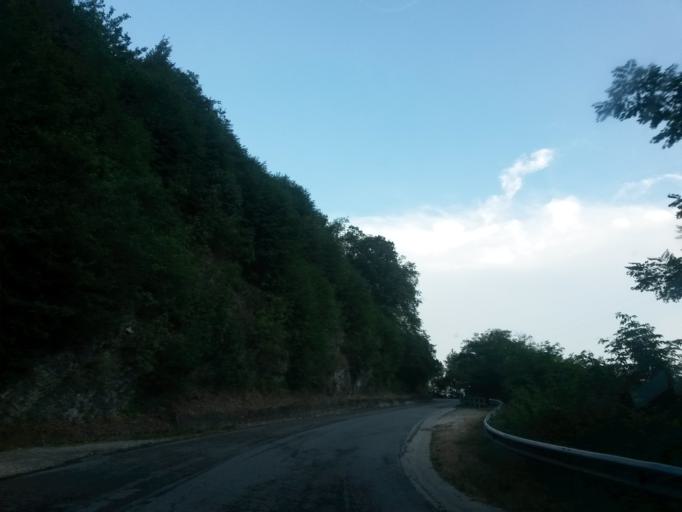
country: IT
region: Lombardy
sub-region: Provincia di Brescia
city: Gardola
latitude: 45.7362
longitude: 10.7172
